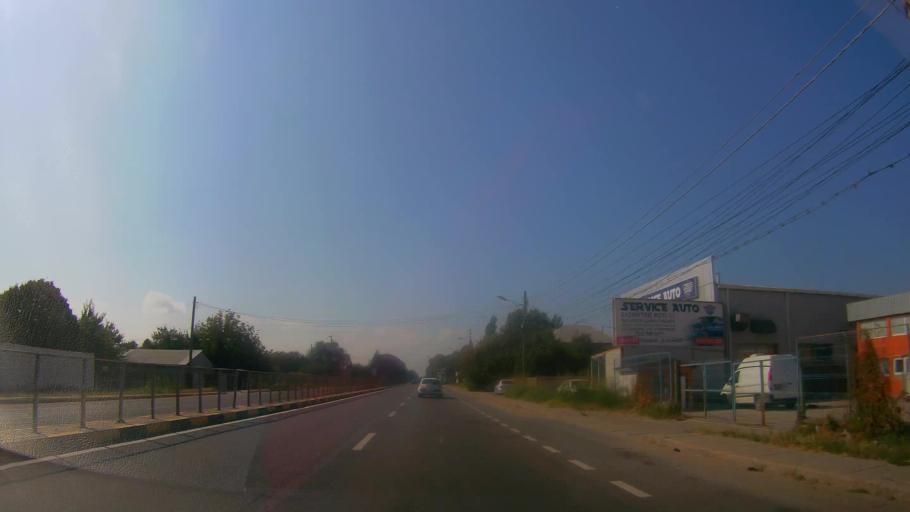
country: RO
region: Giurgiu
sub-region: Comuna Fratesti
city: Remus
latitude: 43.9334
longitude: 25.9764
